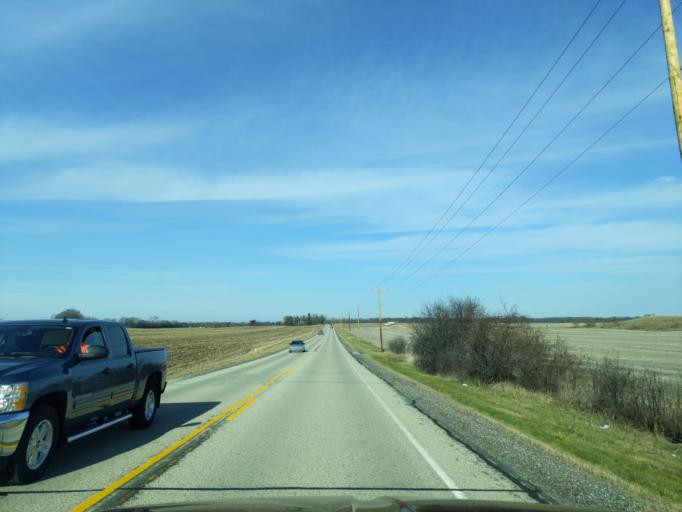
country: US
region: Wisconsin
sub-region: Walworth County
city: Elkhorn
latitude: 42.7379
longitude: -88.5921
